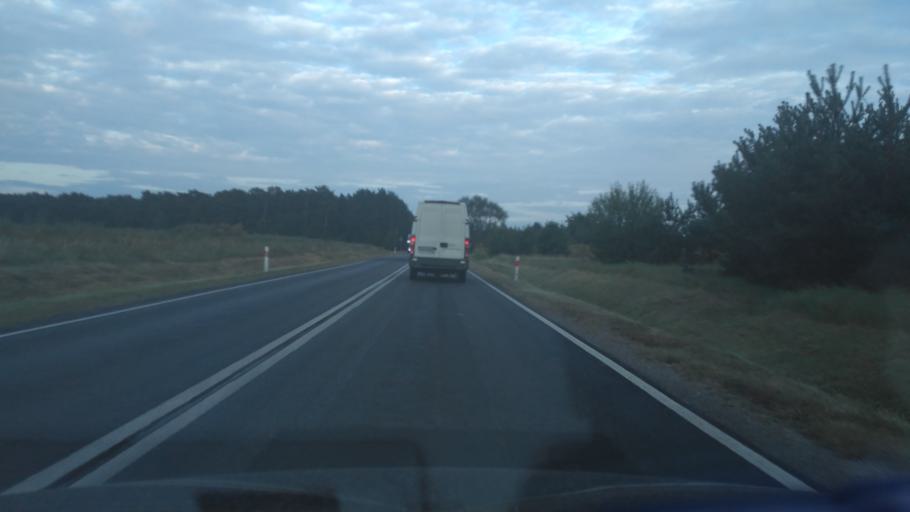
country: PL
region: Lublin Voivodeship
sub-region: Powiat leczynski
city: Spiczyn
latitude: 51.3013
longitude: 22.7476
